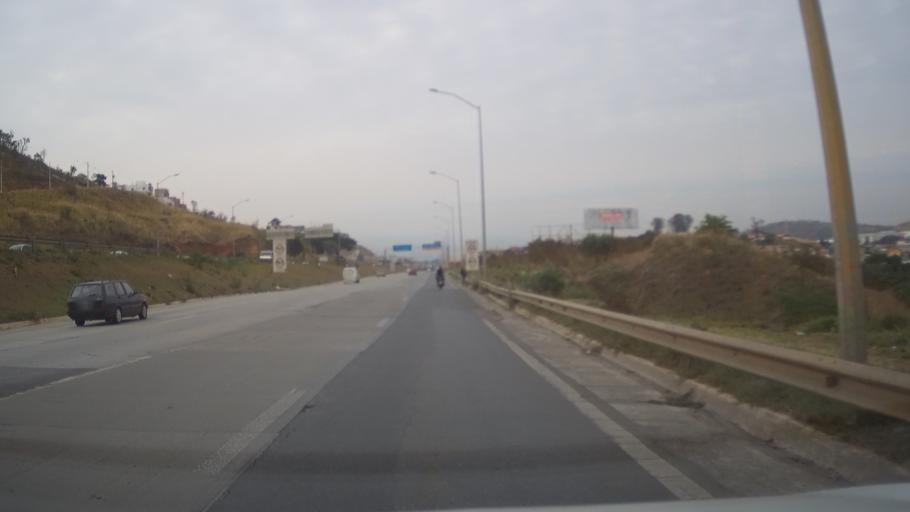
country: BR
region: Minas Gerais
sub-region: Vespasiano
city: Vespasiano
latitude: -19.7636
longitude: -43.9484
